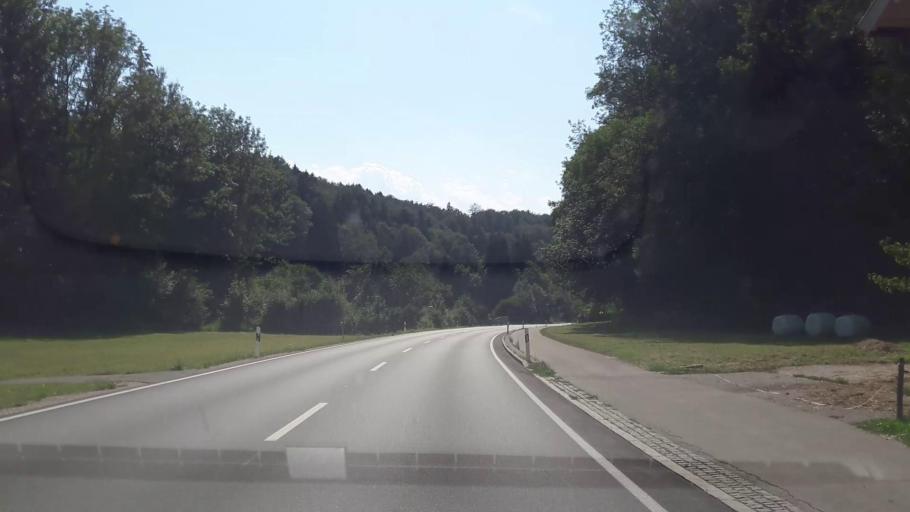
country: DE
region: Bavaria
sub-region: Upper Bavaria
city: Surberg
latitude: 47.8611
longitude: 12.6917
